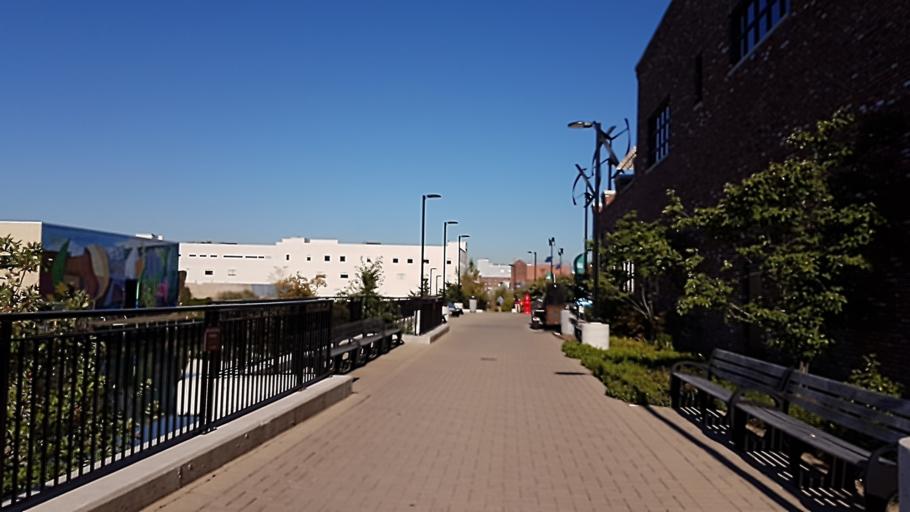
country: US
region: New York
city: New York City
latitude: 40.6745
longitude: -73.9888
